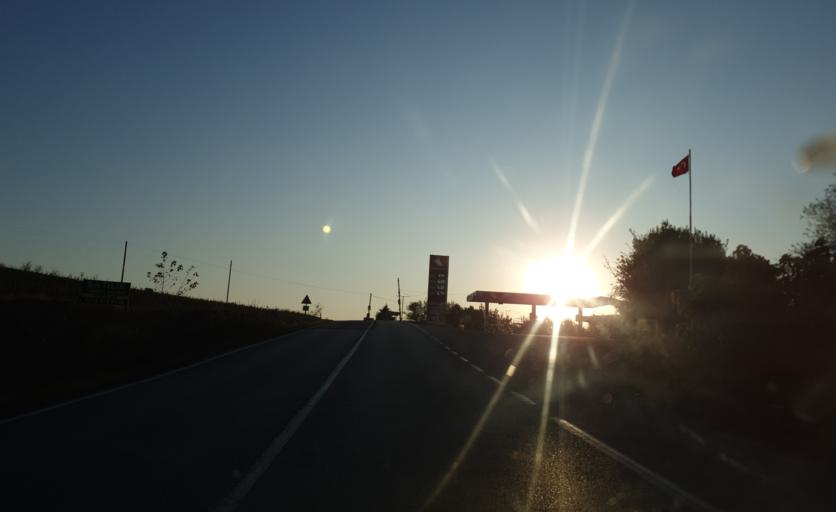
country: TR
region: Tekirdag
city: Beyazkoy
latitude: 41.3453
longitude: 27.7152
